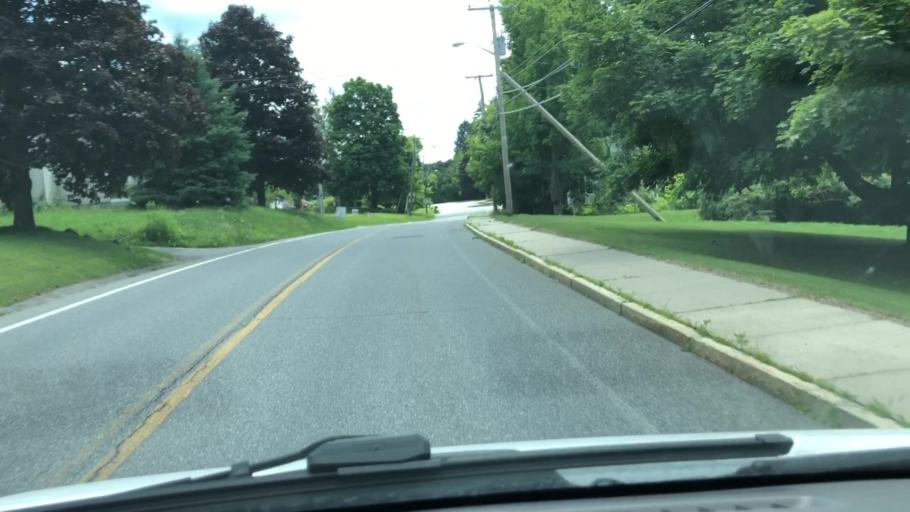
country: US
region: Massachusetts
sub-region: Berkshire County
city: Adams
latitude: 42.6113
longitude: -73.1185
